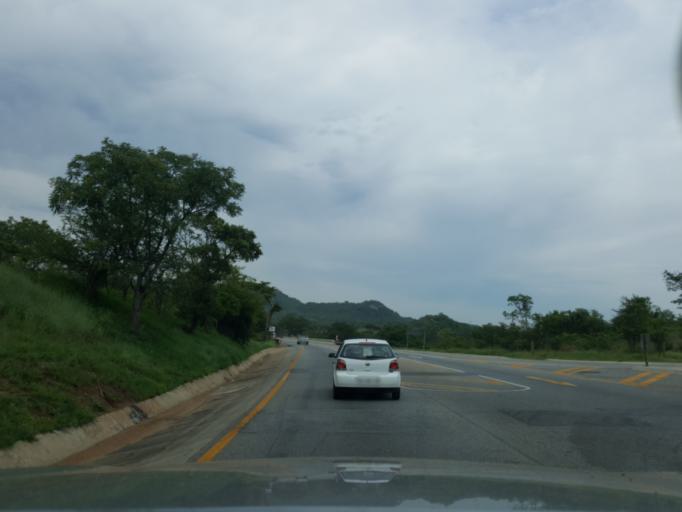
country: ZA
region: Mpumalanga
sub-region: Ehlanzeni District
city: Nelspruit
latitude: -25.4995
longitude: 31.1805
